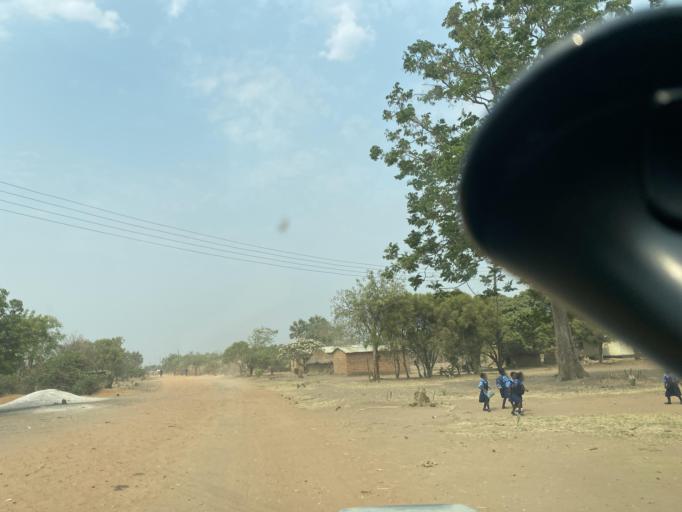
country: ZM
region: Lusaka
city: Kafue
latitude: -15.6653
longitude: 28.0194
